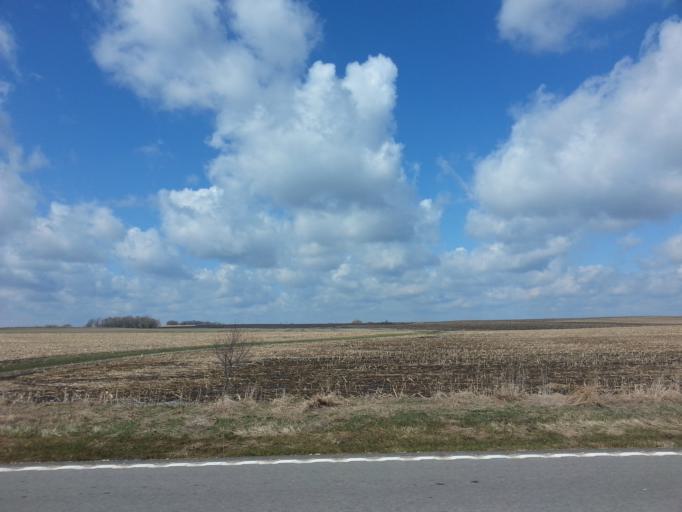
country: US
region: Minnesota
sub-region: Dodge County
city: Dodge Center
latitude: 44.0880
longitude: -92.8815
